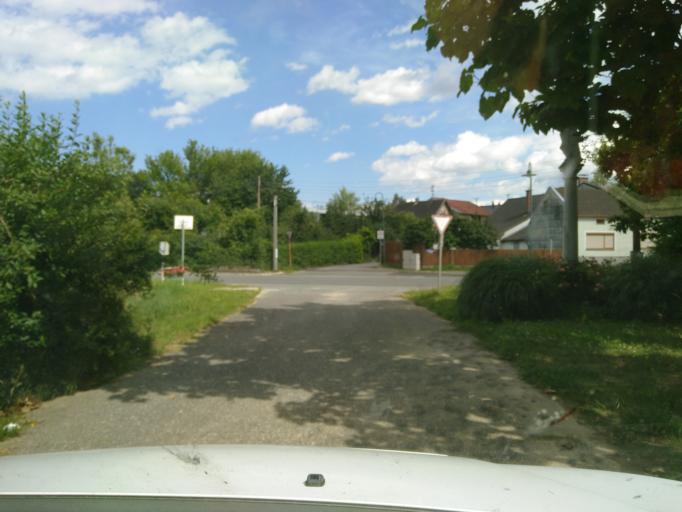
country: AT
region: Burgenland
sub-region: Politischer Bezirk Oberpullendorf
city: Nikitsch
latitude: 47.5296
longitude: 16.6473
